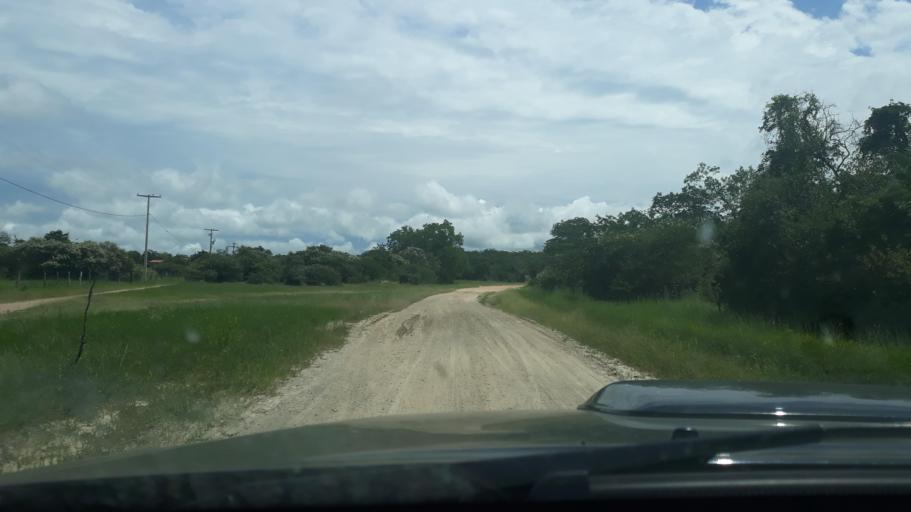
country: BR
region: Bahia
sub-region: Riacho De Santana
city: Riacho de Santana
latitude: -13.8715
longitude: -43.0194
